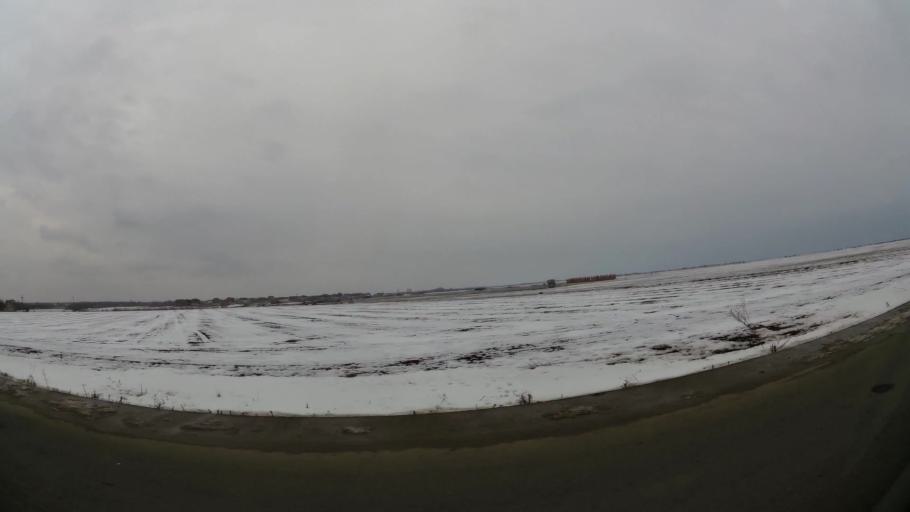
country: RO
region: Ilfov
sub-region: Comuna Tunari
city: Tunari
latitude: 44.5509
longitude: 26.1666
